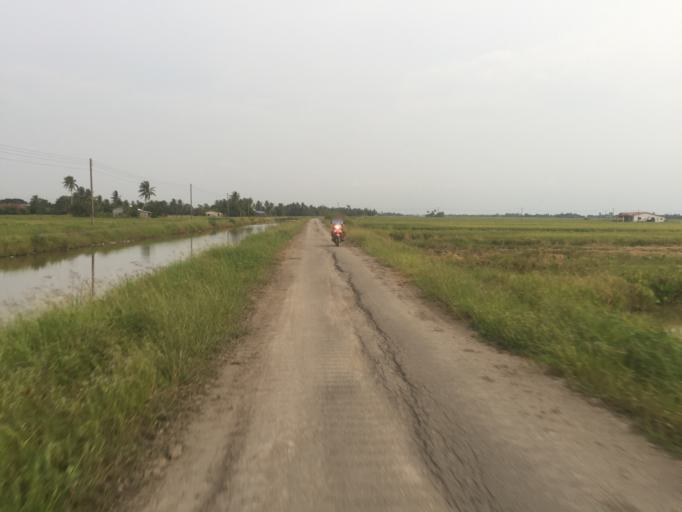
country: MY
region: Kedah
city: Kuala Kedah
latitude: 6.0825
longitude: 100.3119
